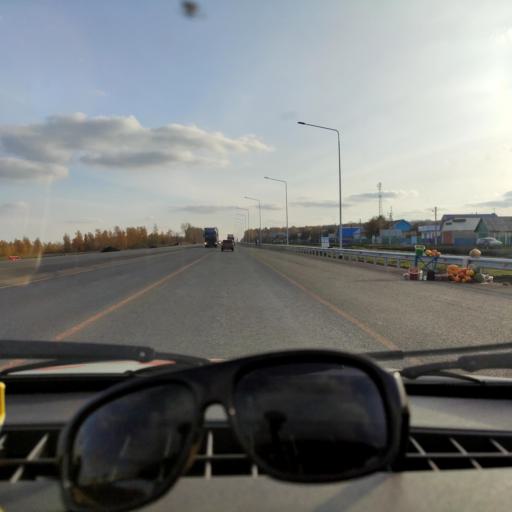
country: RU
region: Bashkortostan
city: Tolbazy
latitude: 54.1278
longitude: 55.9015
